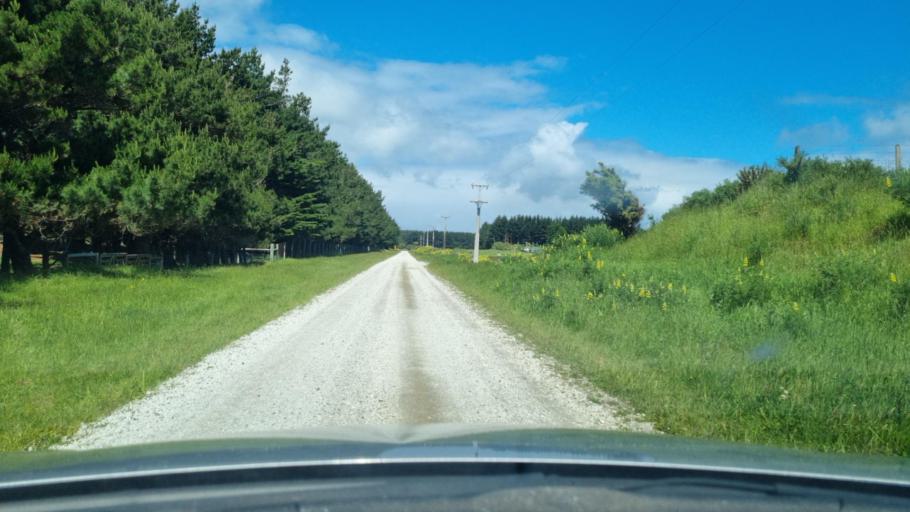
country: NZ
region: Southland
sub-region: Invercargill City
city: Invercargill
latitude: -46.4556
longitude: 168.2743
